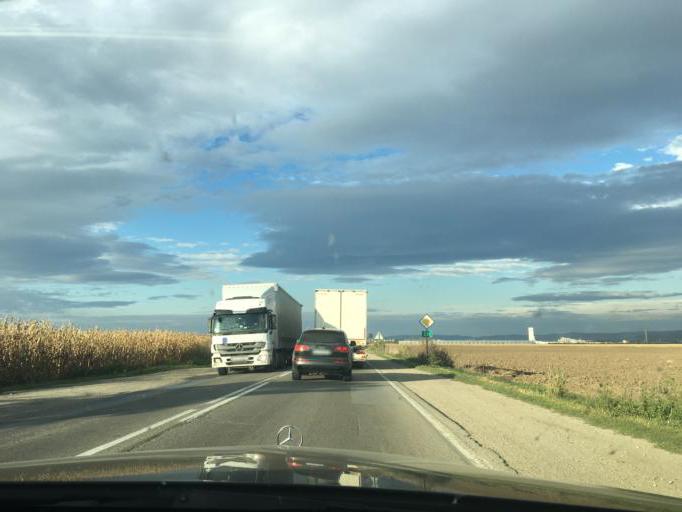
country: RO
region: Alba
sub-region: Oras Teius
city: Teius
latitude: 46.1774
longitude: 23.6550
